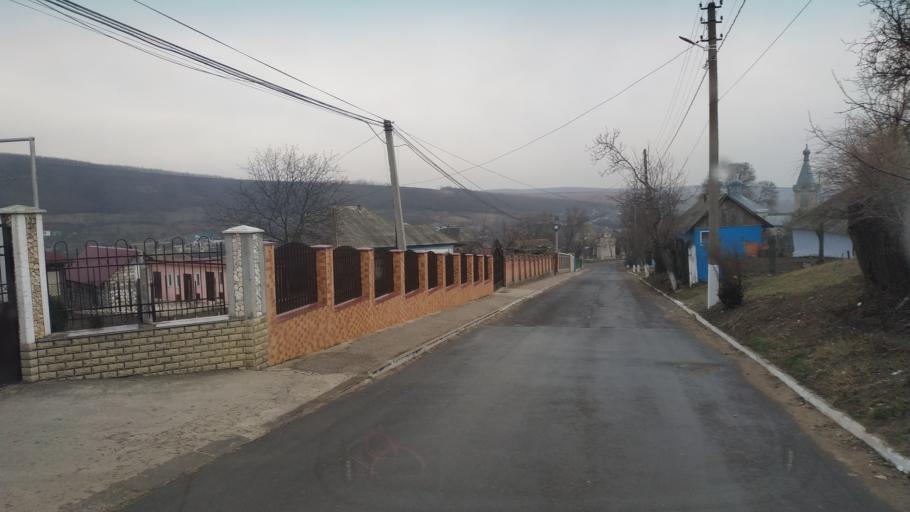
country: MD
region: Chisinau
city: Singera
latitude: 46.8295
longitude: 28.9734
